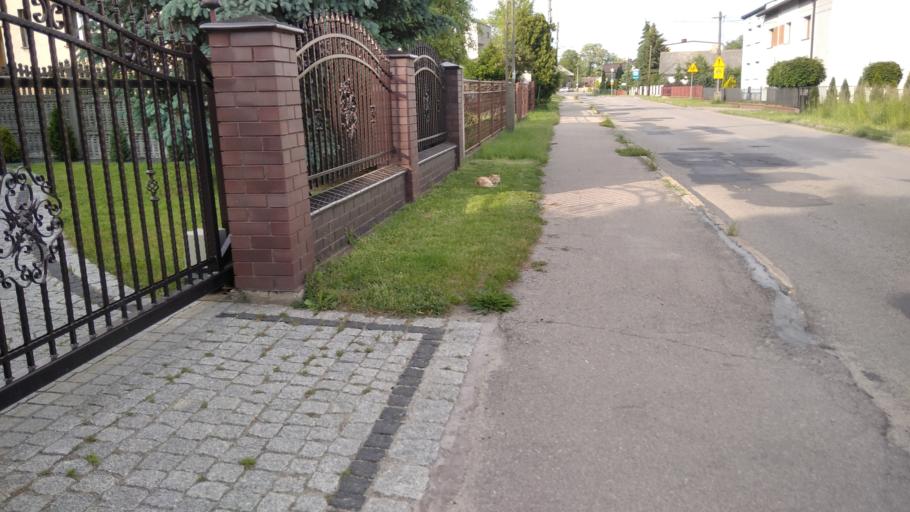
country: PL
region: Silesian Voivodeship
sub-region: Powiat bedzinski
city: Psary
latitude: 50.4043
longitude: 19.1351
